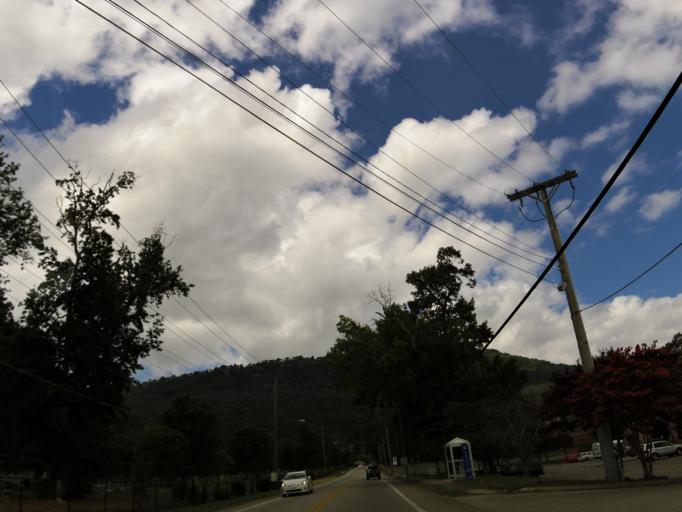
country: US
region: Tennessee
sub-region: Hamilton County
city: Lookout Mountain
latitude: 35.0083
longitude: -85.3222
